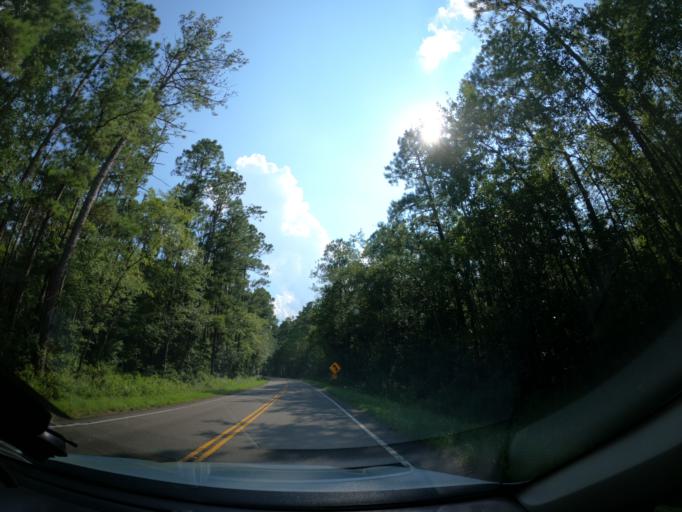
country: US
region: South Carolina
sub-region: Barnwell County
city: Williston
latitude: 33.5516
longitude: -81.4874
